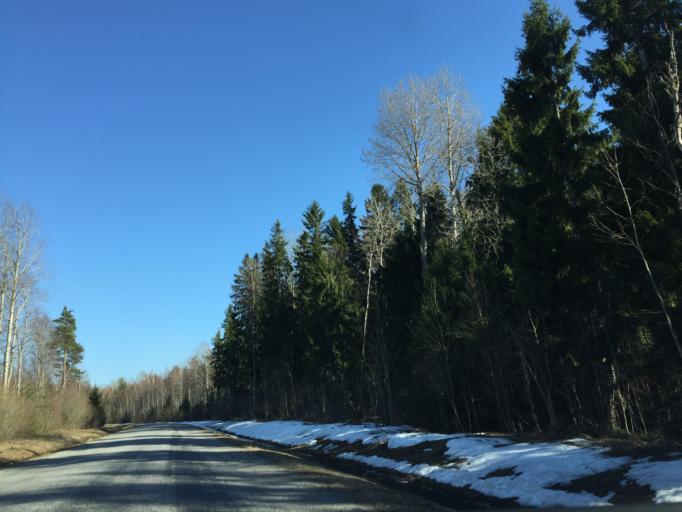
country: RU
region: Pskov
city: Gdov
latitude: 59.0110
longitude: 27.6116
